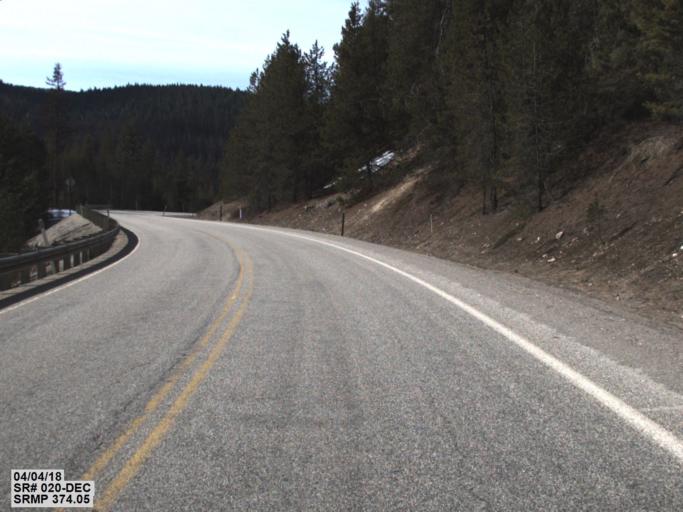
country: US
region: Washington
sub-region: Stevens County
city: Chewelah
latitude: 48.5469
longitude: -117.5750
